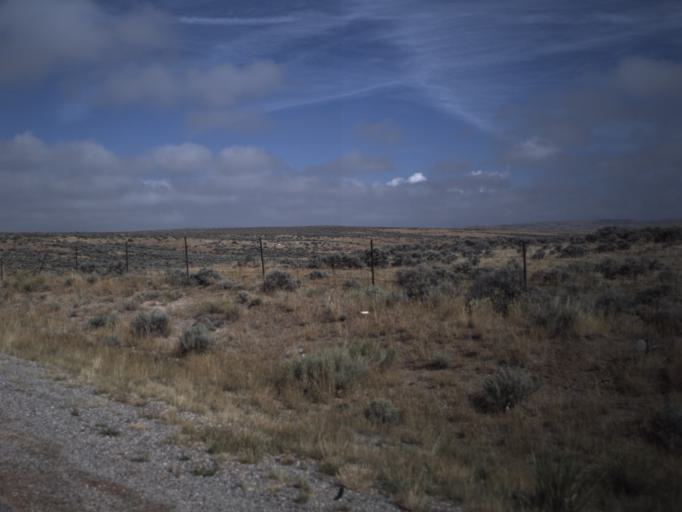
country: US
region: Wyoming
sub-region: Uinta County
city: Evanston
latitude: 41.4416
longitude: -111.0745
